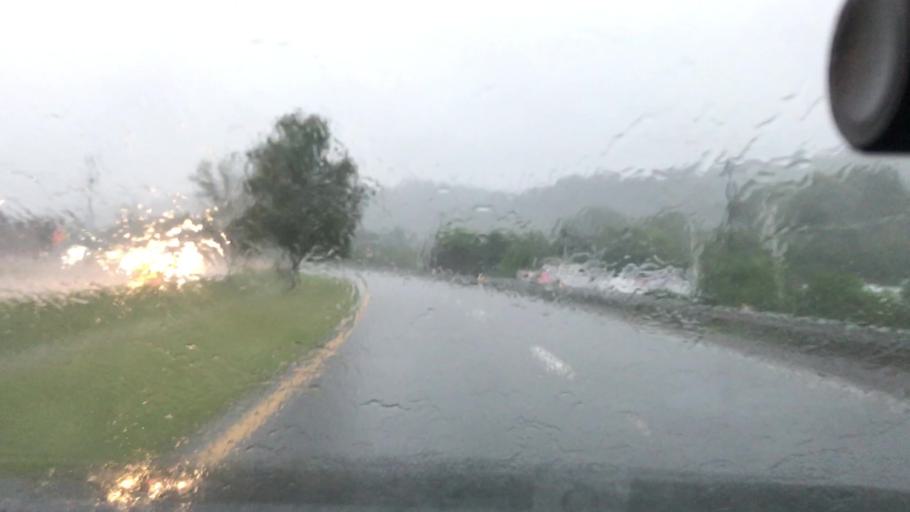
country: US
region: Virginia
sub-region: Giles County
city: Narrows
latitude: 37.3344
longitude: -80.8037
